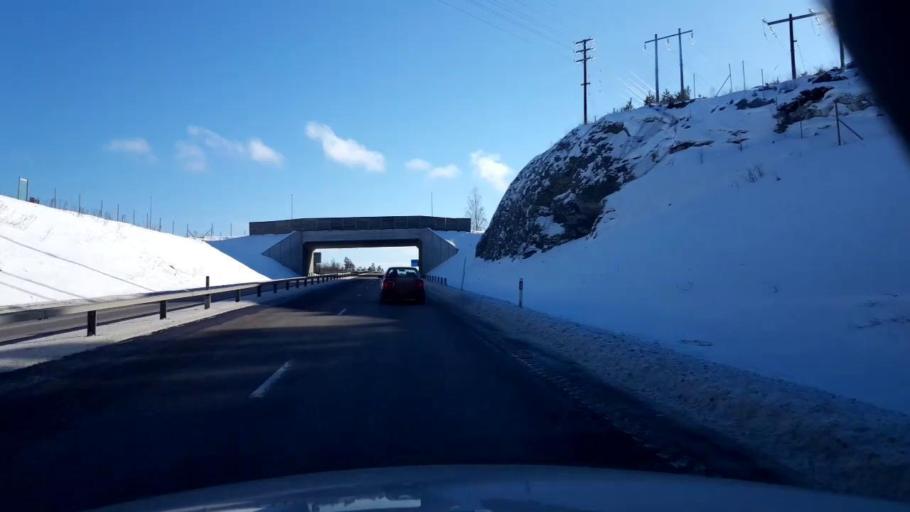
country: SE
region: Vaesternorrland
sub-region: Sundsvalls Kommun
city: Nolby
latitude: 62.2639
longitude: 17.3566
